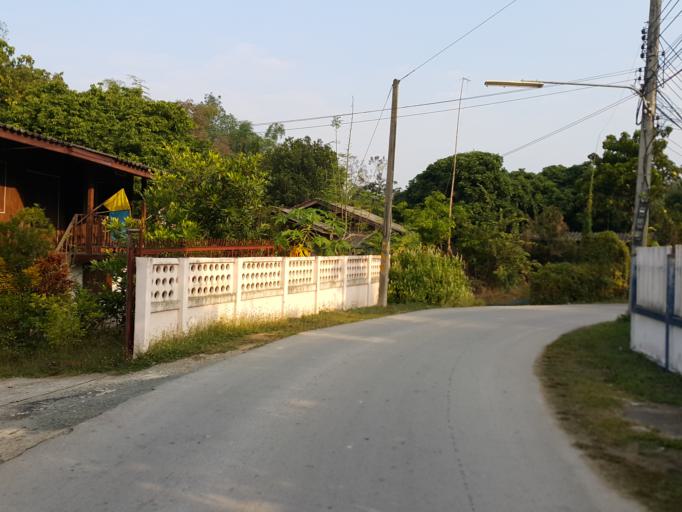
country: TH
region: Chiang Mai
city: San Sai
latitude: 18.8251
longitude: 99.1049
